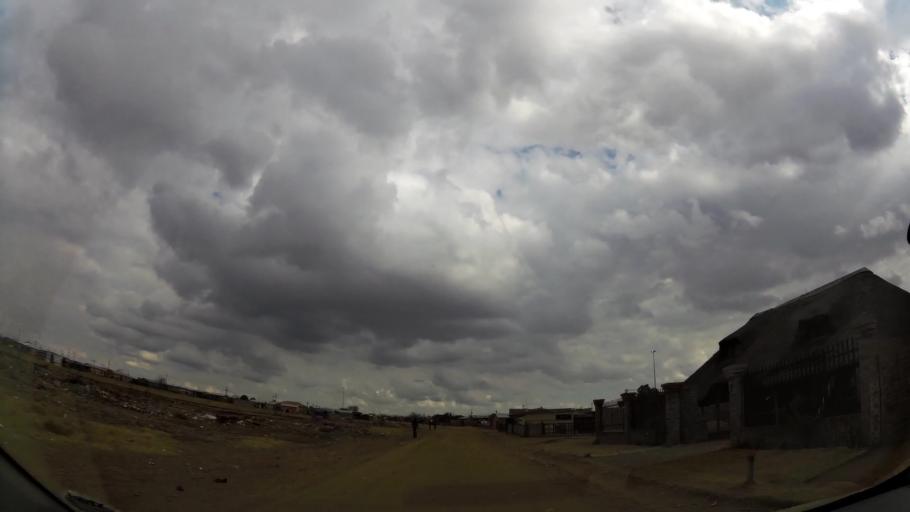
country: ZA
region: Orange Free State
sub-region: Fezile Dabi District Municipality
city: Sasolburg
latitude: -26.8602
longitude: 27.8660
